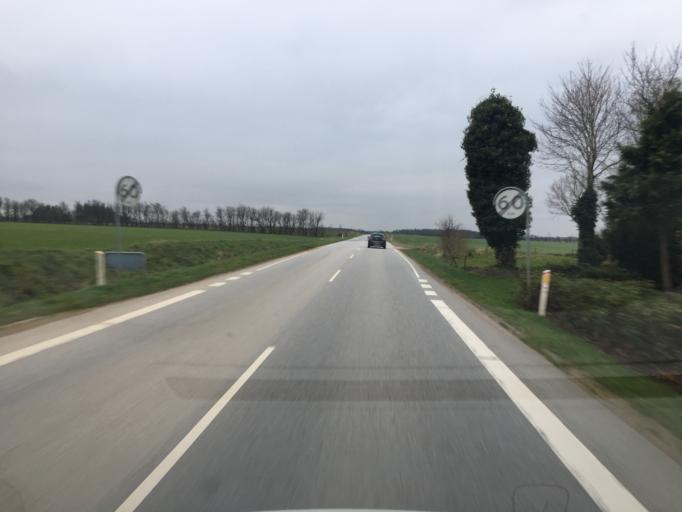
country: DK
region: South Denmark
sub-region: Aabenraa Kommune
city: Tinglev
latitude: 55.0061
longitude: 9.2501
